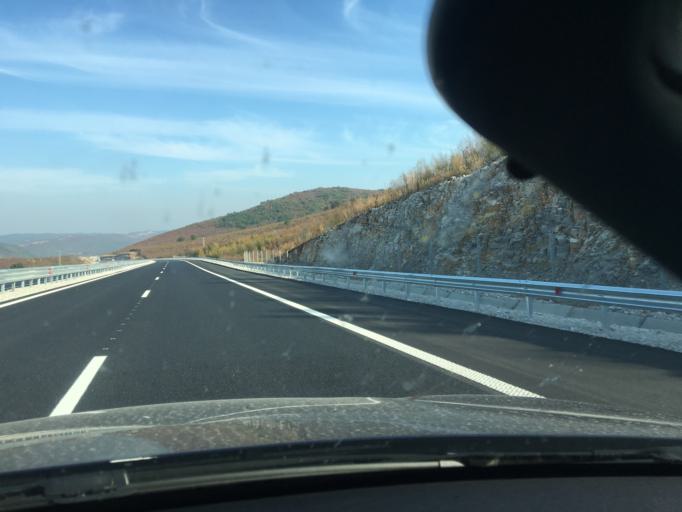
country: BG
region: Lovech
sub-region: Obshtina Yablanitsa
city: Yablanitsa
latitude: 43.0526
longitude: 24.1811
